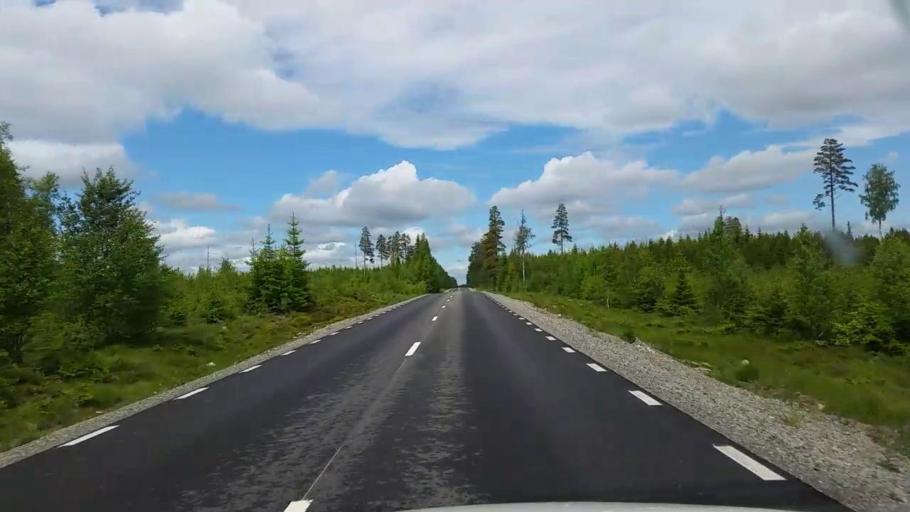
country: SE
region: Gaevleborg
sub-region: Sandvikens Kommun
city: Jarbo
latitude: 60.9044
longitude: 16.3773
